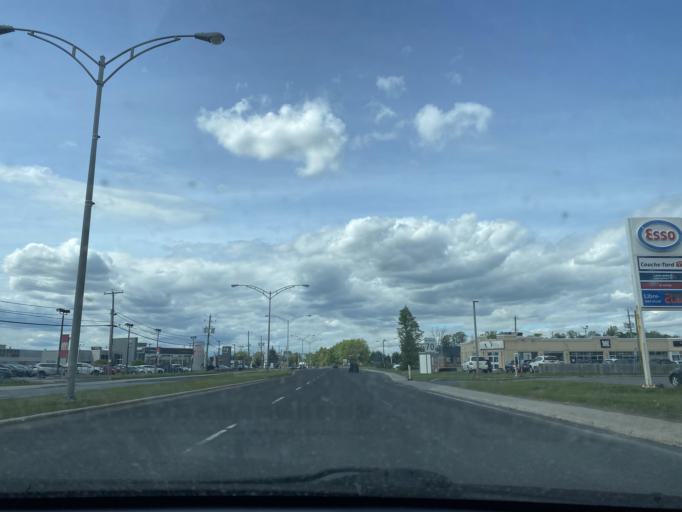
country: CA
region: Quebec
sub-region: Monteregie
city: Carignan
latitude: 45.4544
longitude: -73.3018
